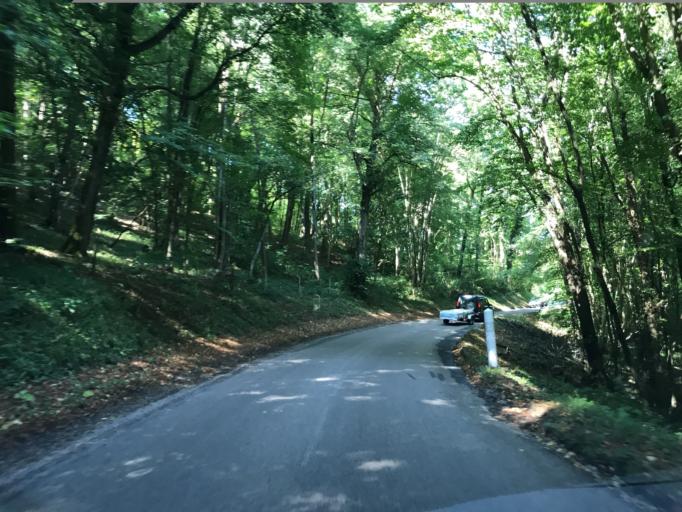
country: FR
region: Haute-Normandie
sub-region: Departement de l'Eure
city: Heudreville-sur-Eure
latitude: 49.1103
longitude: 1.2104
